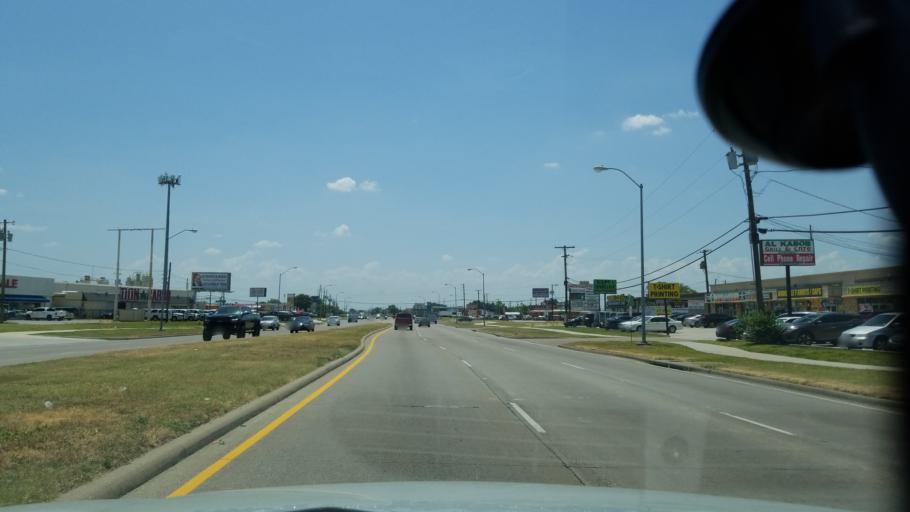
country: US
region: Texas
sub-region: Dallas County
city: Farmers Branch
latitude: 32.8946
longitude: -96.8912
